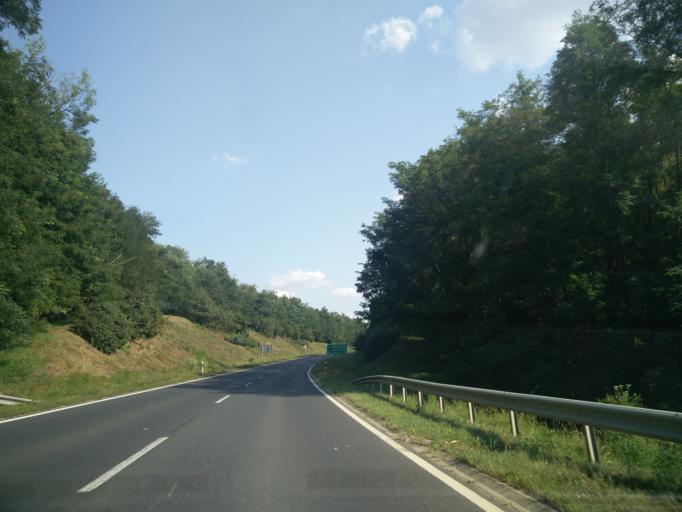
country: HU
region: Zala
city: Zalaegerszeg
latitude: 46.8784
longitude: 16.8490
